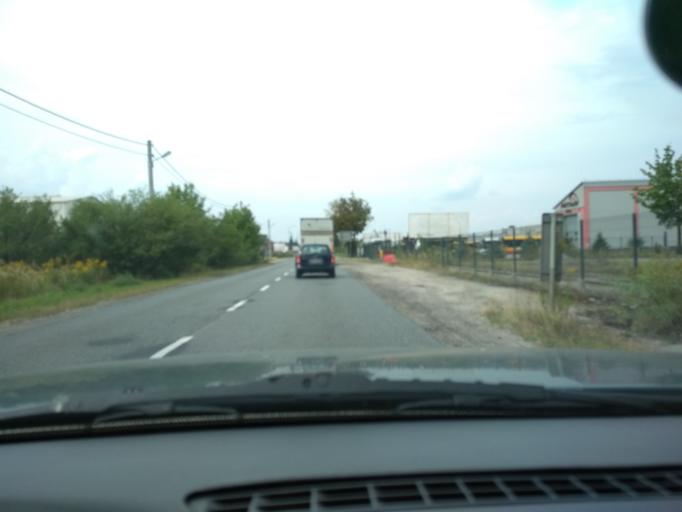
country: PL
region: Silesian Voivodeship
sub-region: Powiat zawiercianski
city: Zawiercie
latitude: 50.4710
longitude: 19.4043
